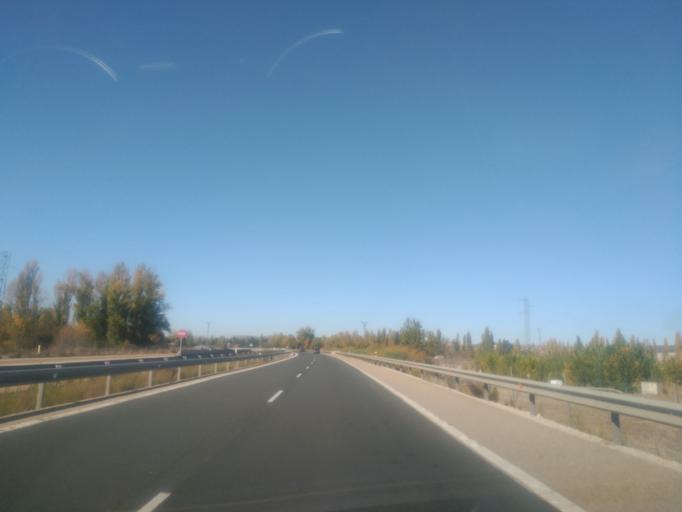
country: ES
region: Castille and Leon
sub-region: Provincia de Valladolid
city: Tudela de Duero
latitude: 41.5934
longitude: -4.5764
